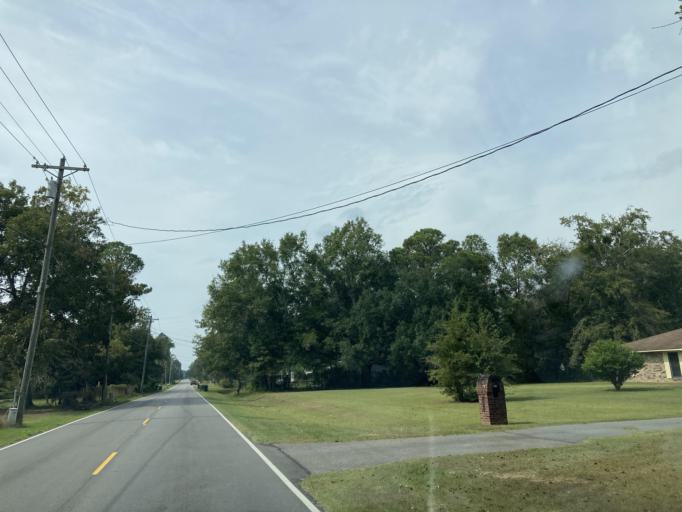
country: US
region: Mississippi
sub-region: Jackson County
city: Gulf Hills
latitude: 30.4504
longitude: -88.8468
